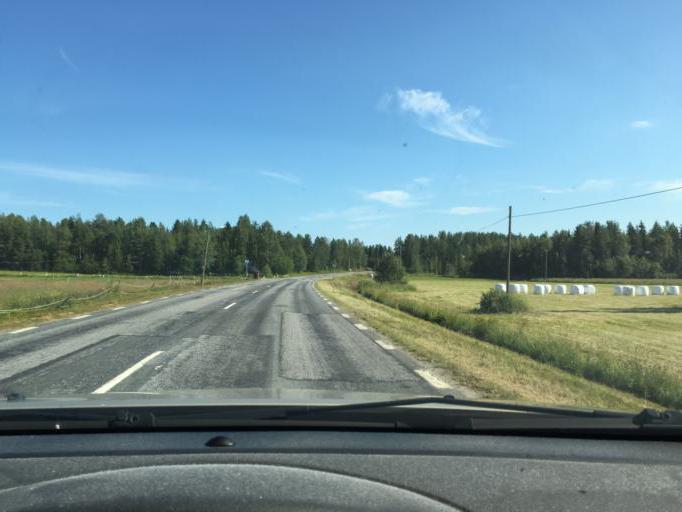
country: SE
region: Norrbotten
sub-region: Bodens Kommun
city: Boden
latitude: 65.9150
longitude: 21.8466
